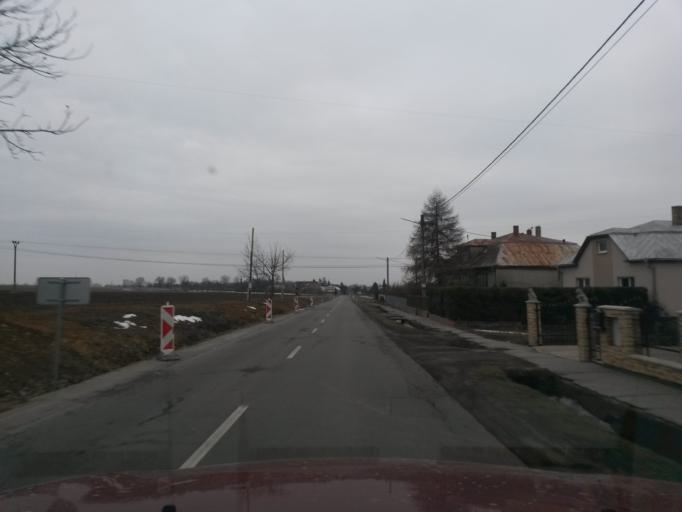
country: SK
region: Kosicky
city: Trebisov
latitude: 48.6922
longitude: 21.8096
